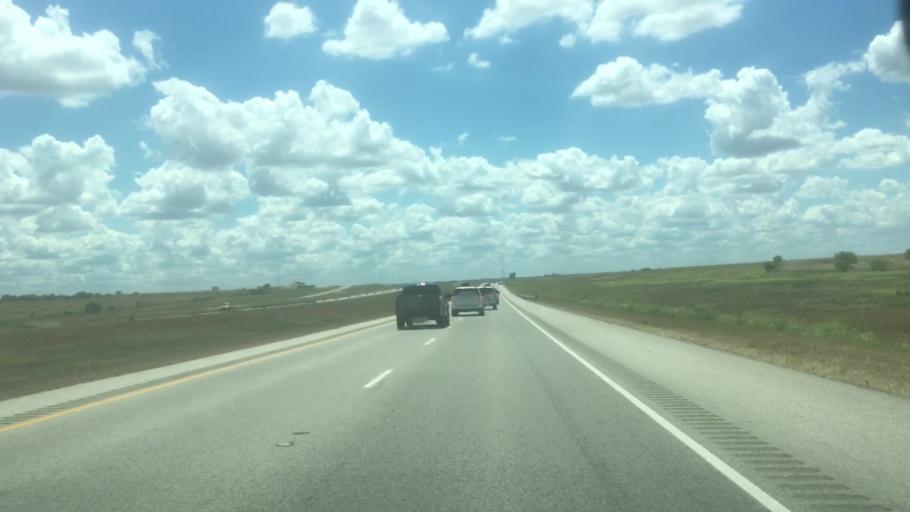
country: US
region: Texas
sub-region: Caldwell County
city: Martindale
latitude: 29.7947
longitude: -97.7820
